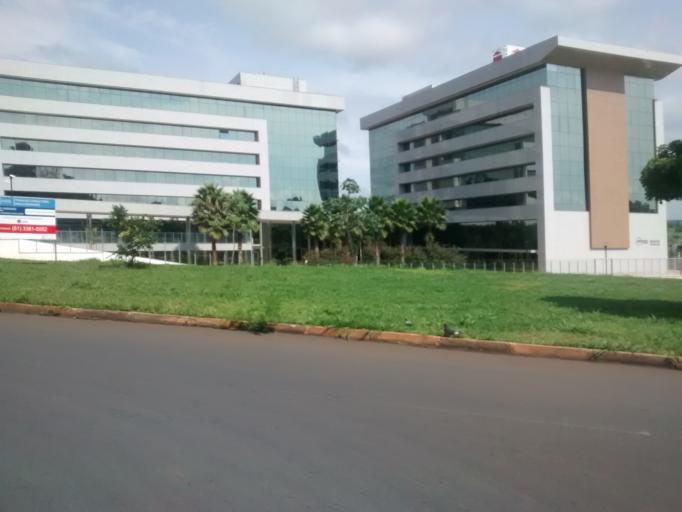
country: BR
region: Federal District
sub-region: Brasilia
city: Brasilia
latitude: -15.7367
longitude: -47.8937
